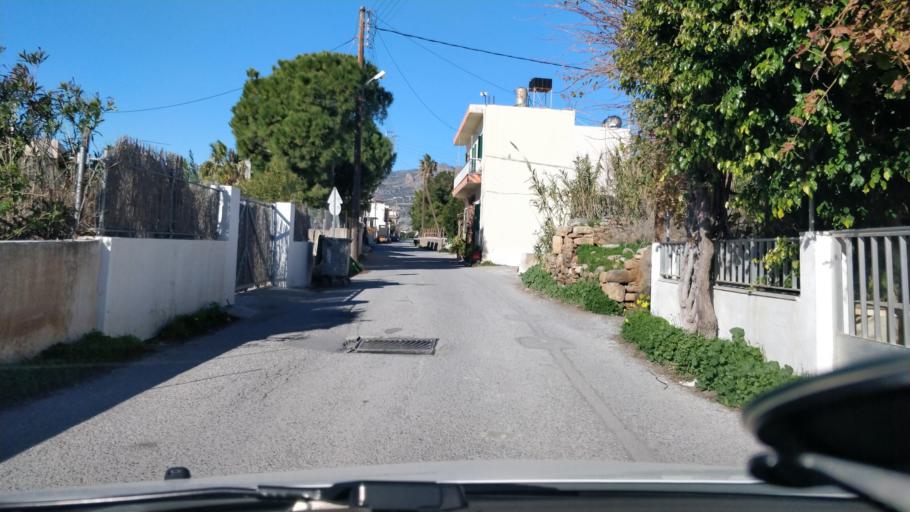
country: GR
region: Crete
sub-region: Nomos Lasithiou
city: Gra Liyia
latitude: 35.0156
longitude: 25.6918
